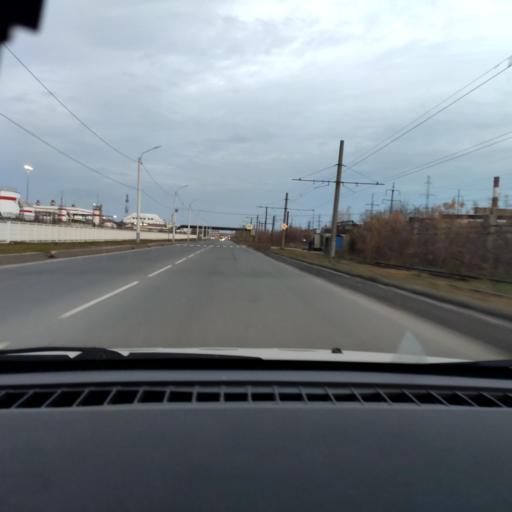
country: RU
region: Perm
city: Gamovo
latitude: 57.9184
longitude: 56.1484
